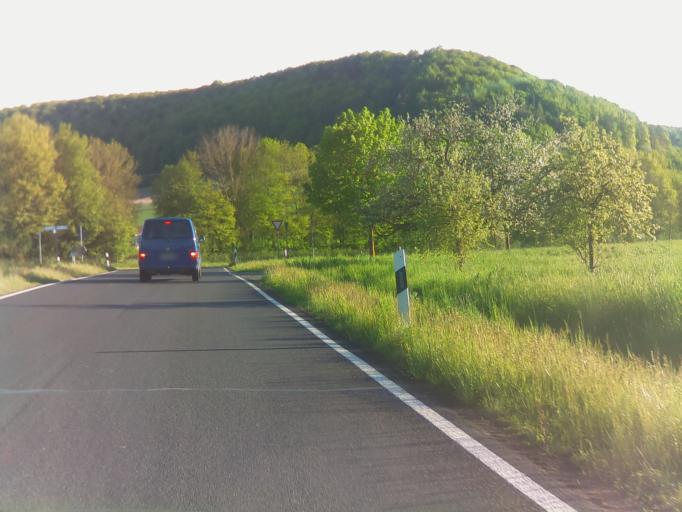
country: DE
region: Bavaria
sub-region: Regierungsbezirk Unterfranken
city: Ramsthal
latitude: 50.1431
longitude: 10.0457
